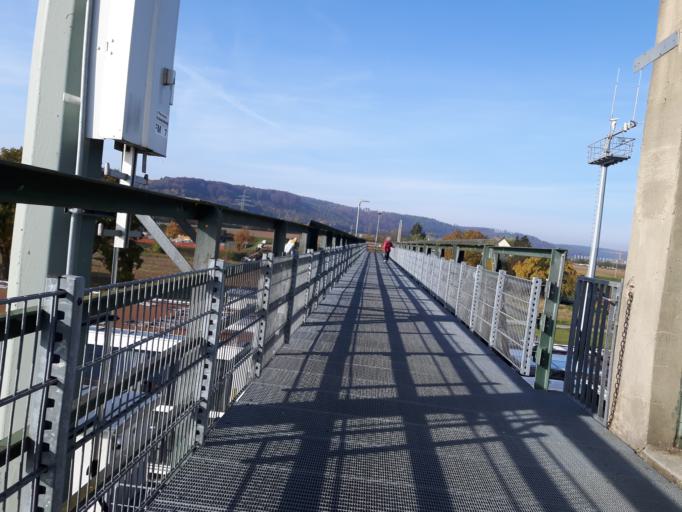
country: DE
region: Bavaria
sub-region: Regierungsbezirk Unterfranken
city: Kleinwallstadt
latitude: 49.8686
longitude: 9.1603
